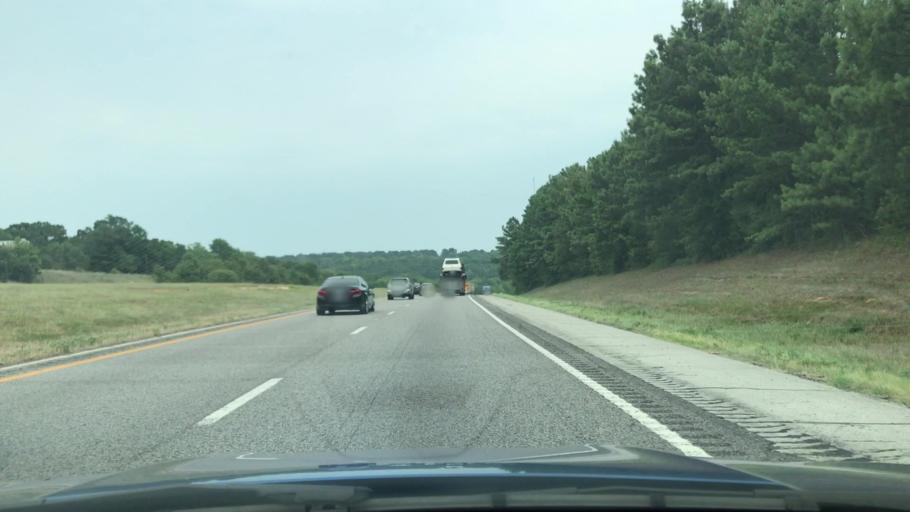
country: US
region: Texas
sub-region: Smith County
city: Lindale
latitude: 32.4685
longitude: -95.3492
